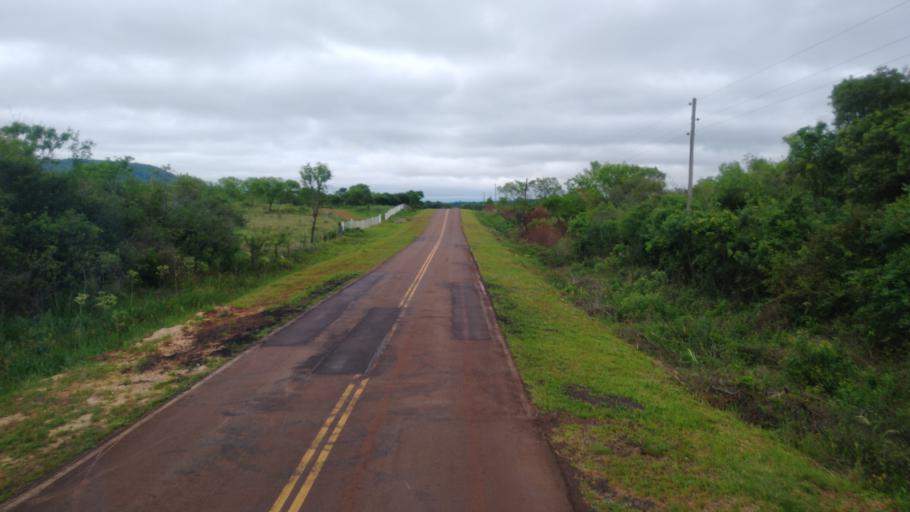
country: AR
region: Misiones
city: Santa Ana
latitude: -27.4102
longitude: -55.5562
